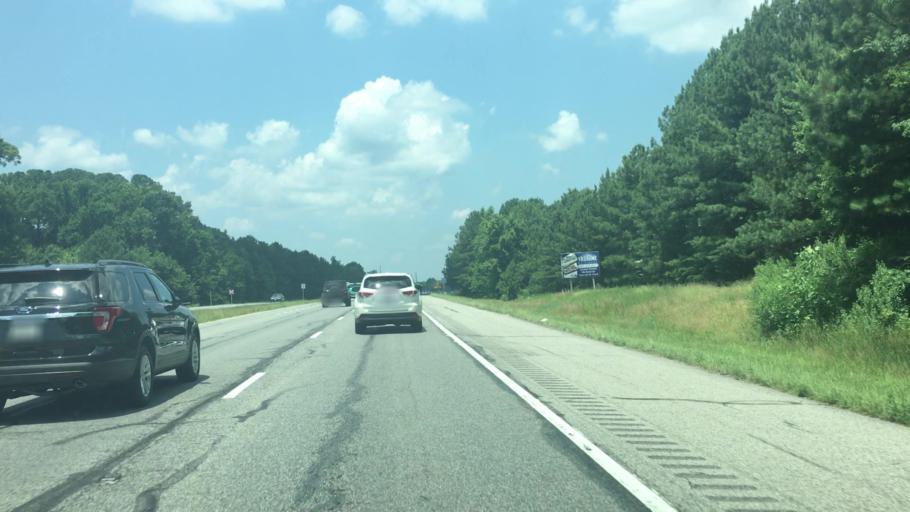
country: US
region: Maryland
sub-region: Saint Mary's County
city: California
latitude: 38.3275
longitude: -76.5516
